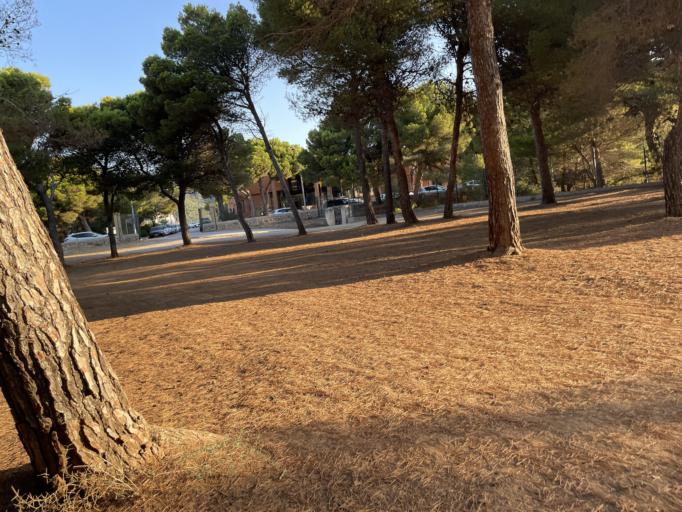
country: ES
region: Balearic Islands
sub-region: Illes Balears
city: Capdepera
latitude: 39.7174
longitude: 3.4640
